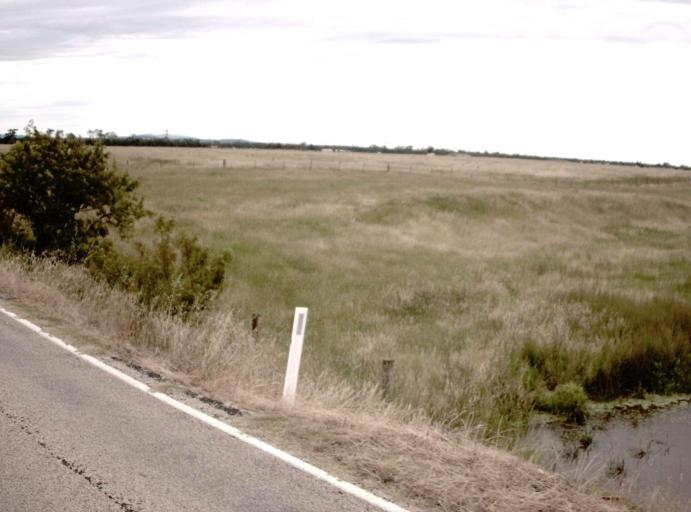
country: AU
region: Victoria
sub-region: East Gippsland
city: Bairnsdale
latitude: -37.8564
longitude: 147.5644
